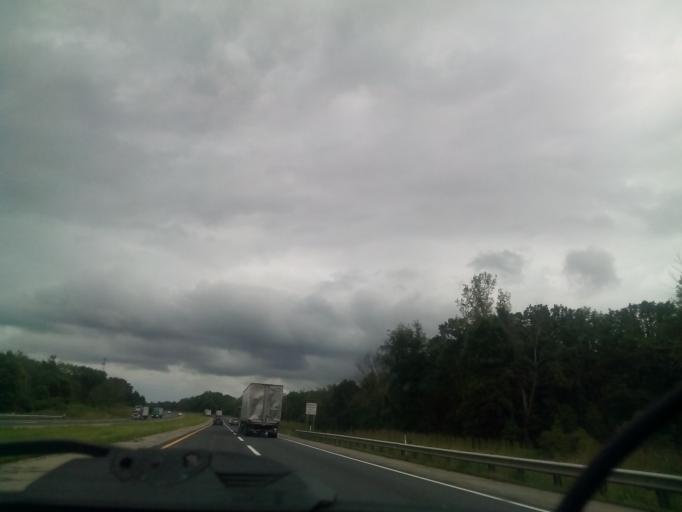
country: US
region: Indiana
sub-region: Steuben County
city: Fremont
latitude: 41.6535
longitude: -84.8439
